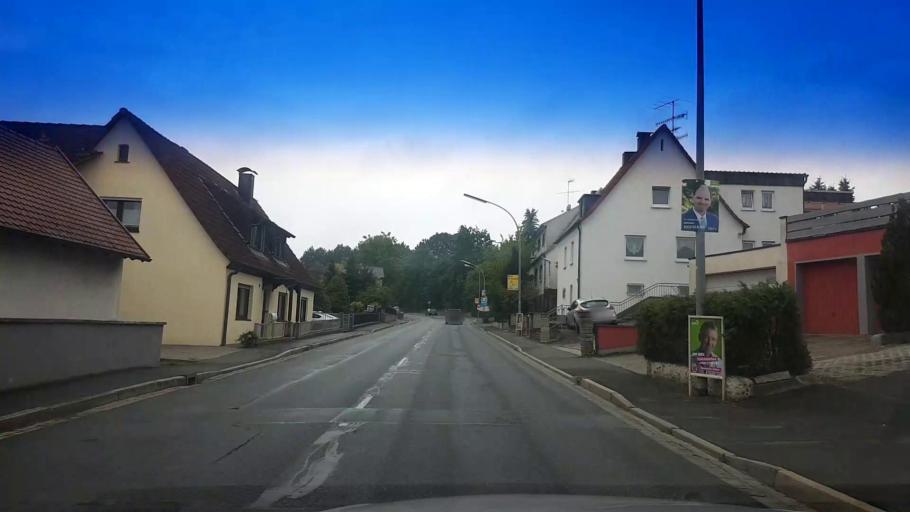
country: DE
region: Bavaria
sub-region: Upper Franconia
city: Forchheim
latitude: 49.7143
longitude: 11.0424
